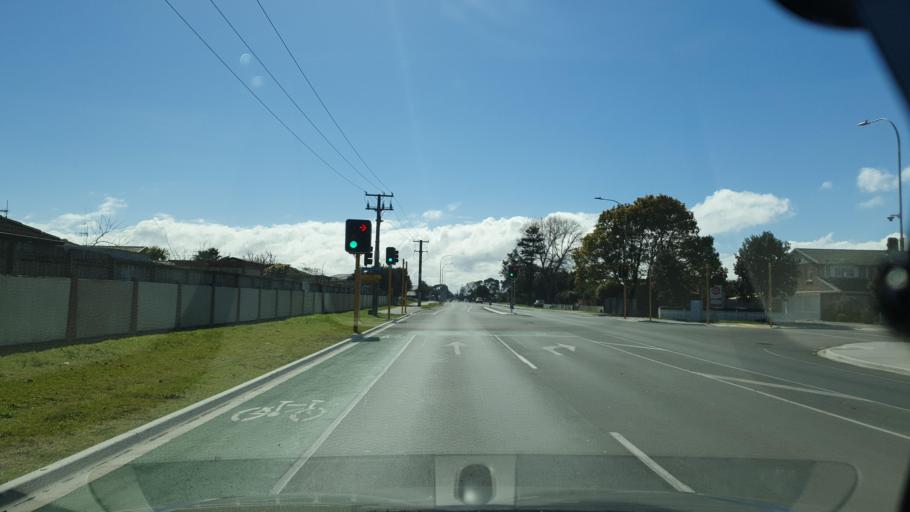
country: NZ
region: Bay of Plenty
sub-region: Tauranga City
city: Tauranga
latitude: -37.7075
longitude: 176.2847
